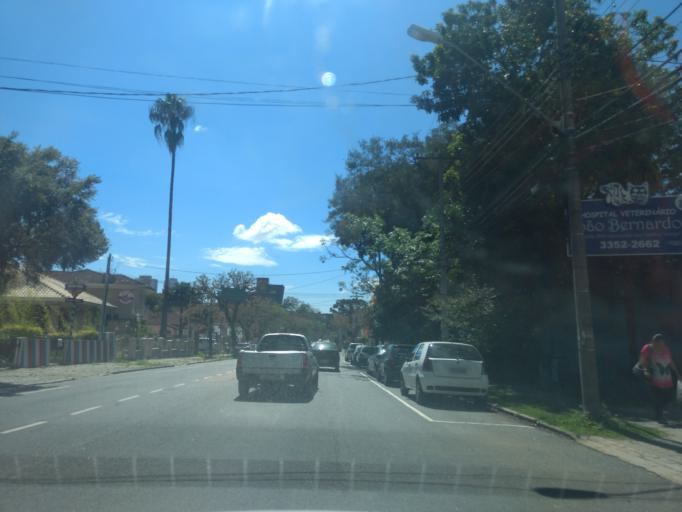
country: BR
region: Parana
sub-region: Curitiba
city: Curitiba
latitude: -25.4100
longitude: -49.2531
